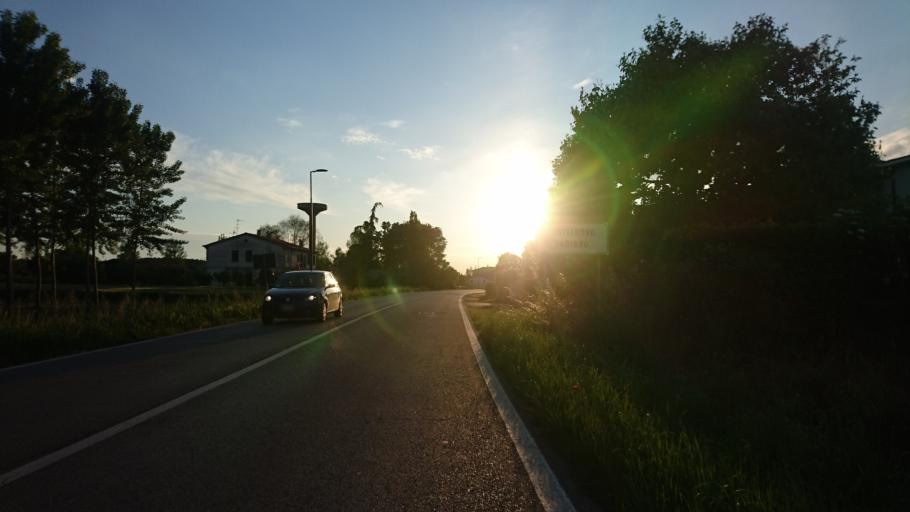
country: IT
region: Veneto
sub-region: Provincia di Rovigo
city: Castelnovo Bariano
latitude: 45.0238
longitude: 11.2996
